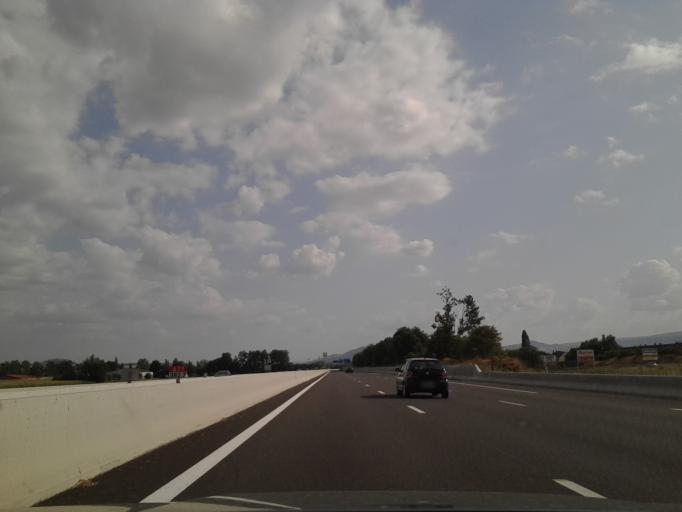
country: FR
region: Auvergne
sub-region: Departement du Puy-de-Dome
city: Gerzat
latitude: 45.8257
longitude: 3.1579
